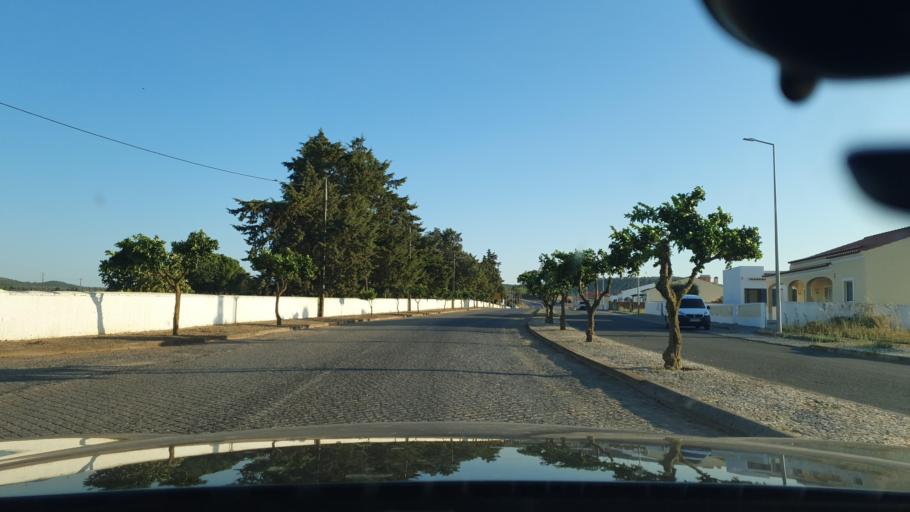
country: PT
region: Portalegre
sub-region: Fronteira
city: Fronteira
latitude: 38.9486
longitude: -7.6757
